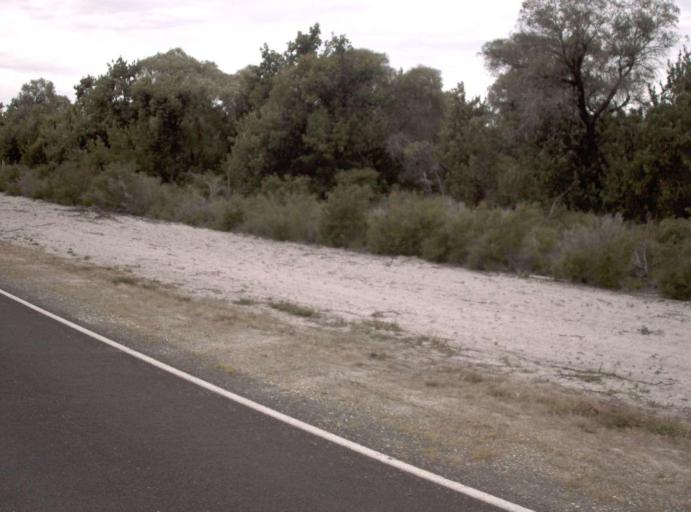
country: AU
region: Victoria
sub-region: Wellington
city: Sale
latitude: -38.1725
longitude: 147.3832
